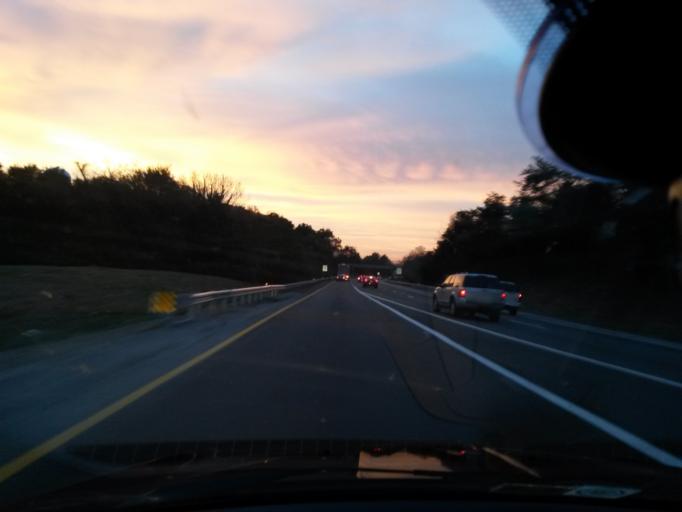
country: US
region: Virginia
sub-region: Roanoke County
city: Hollins
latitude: 37.3382
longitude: -79.9969
